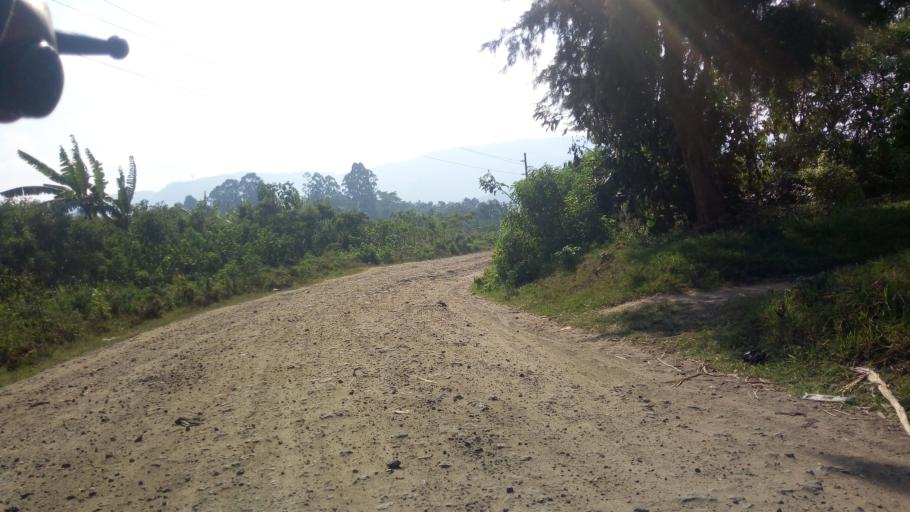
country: UG
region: Western Region
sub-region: Kisoro District
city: Kisoro
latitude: -1.2253
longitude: 29.7136
